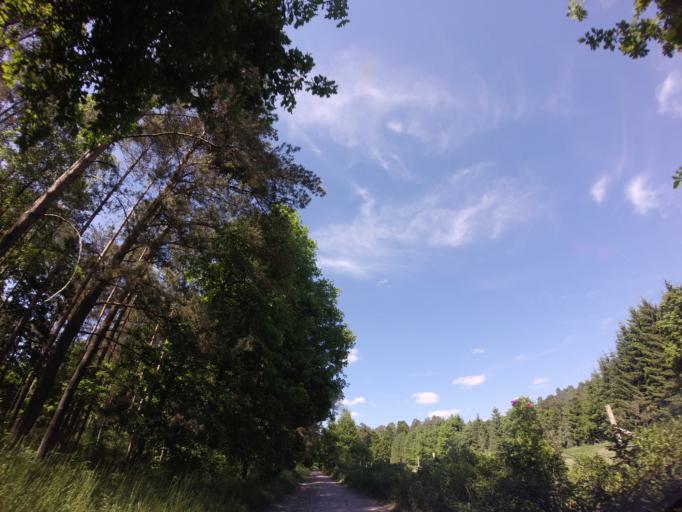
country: PL
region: West Pomeranian Voivodeship
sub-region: Powiat choszczenski
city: Drawno
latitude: 53.1662
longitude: 15.7916
